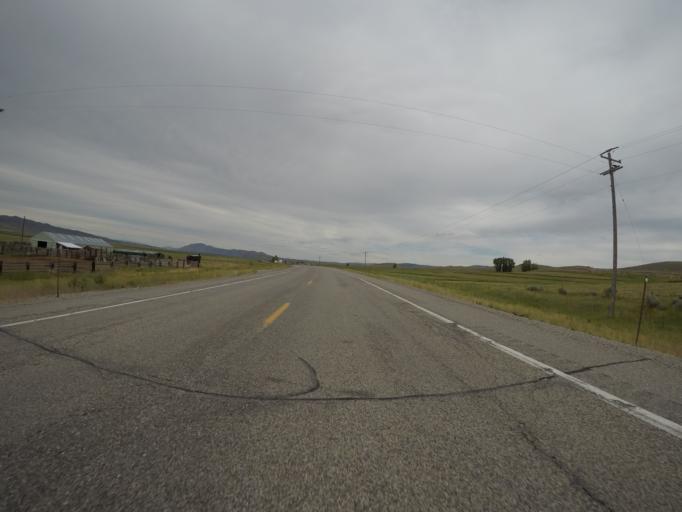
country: US
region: Utah
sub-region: Rich County
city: Randolph
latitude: 41.9984
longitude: -110.9375
